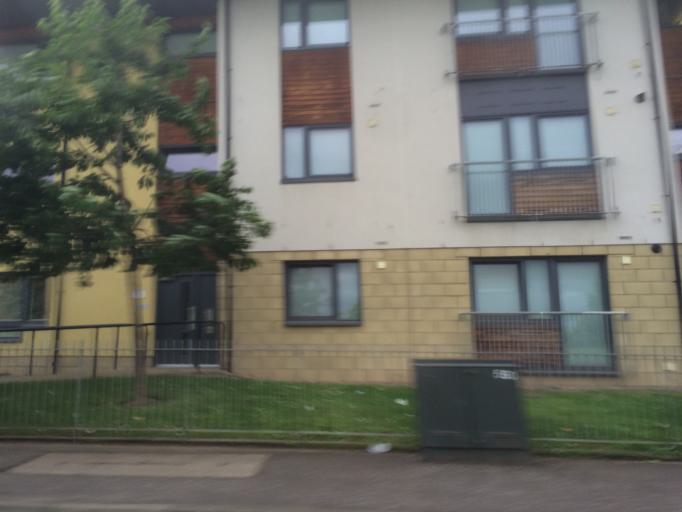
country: GB
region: Scotland
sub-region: Perth and Kinross
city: Perth
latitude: 56.4063
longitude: -3.4577
